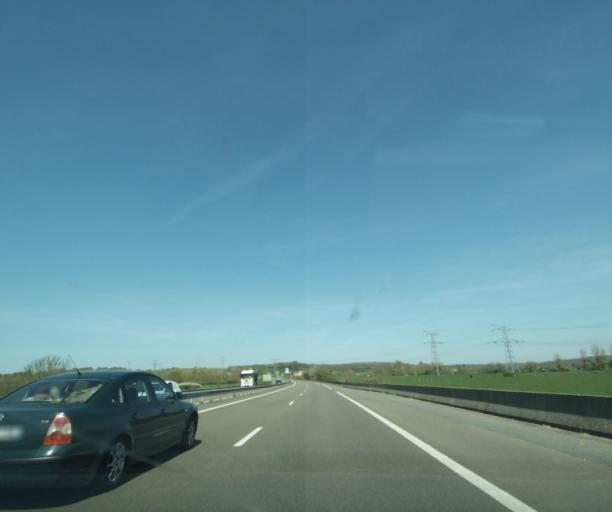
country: FR
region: Bourgogne
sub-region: Departement de la Nievre
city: Coulanges-les-Nevers
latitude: 47.0051
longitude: 3.2048
